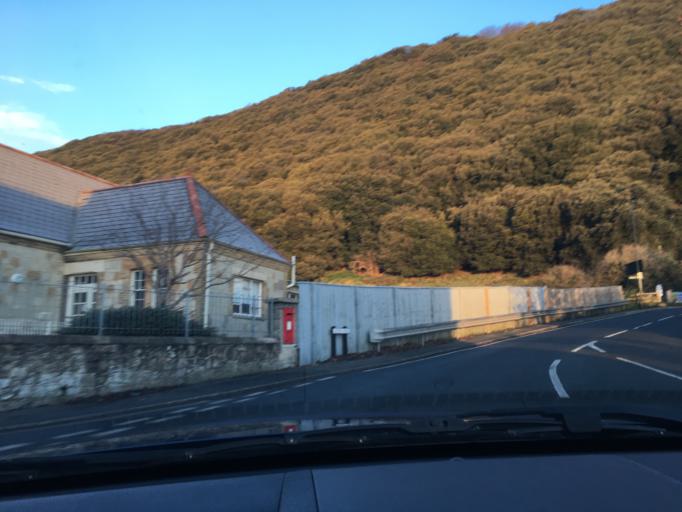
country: GB
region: England
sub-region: Isle of Wight
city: Ventnor
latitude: 50.5984
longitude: -1.1971
